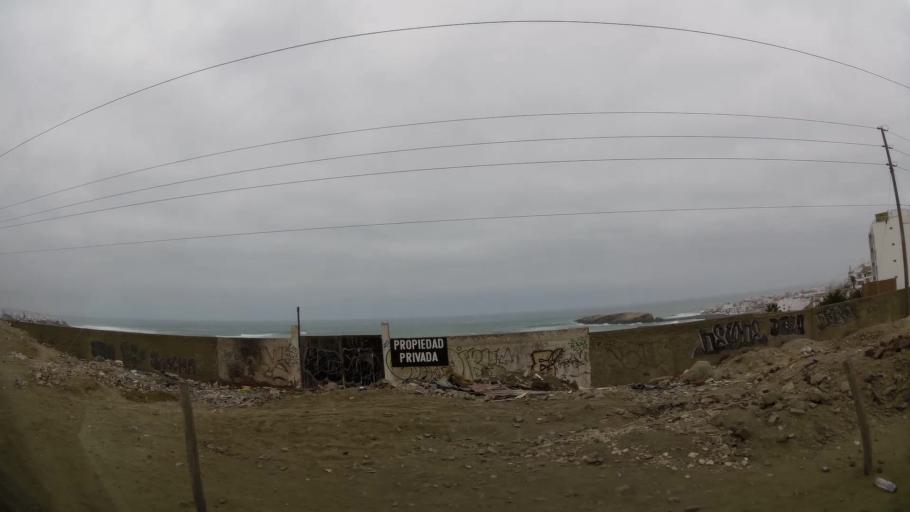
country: PE
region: Lima
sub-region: Lima
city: Punta Hermosa
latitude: -12.3387
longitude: -76.8173
